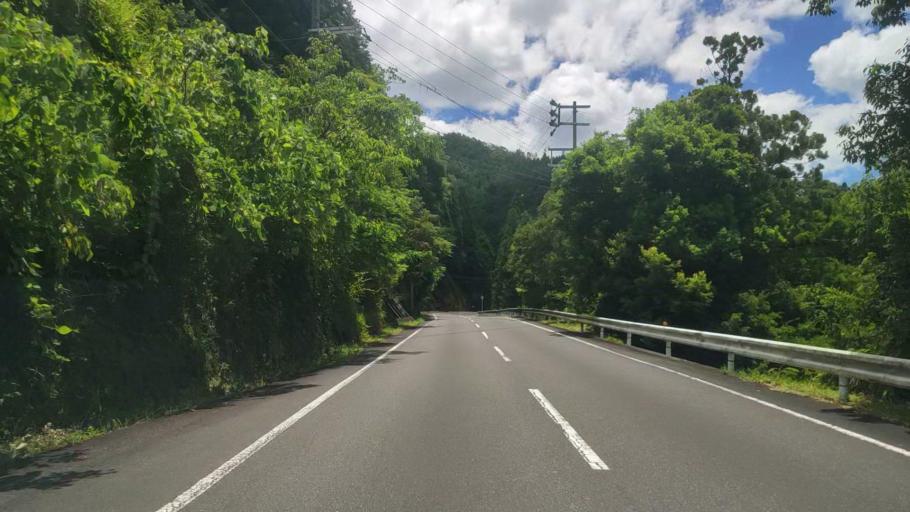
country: JP
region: Mie
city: Owase
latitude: 33.9705
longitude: 136.0609
